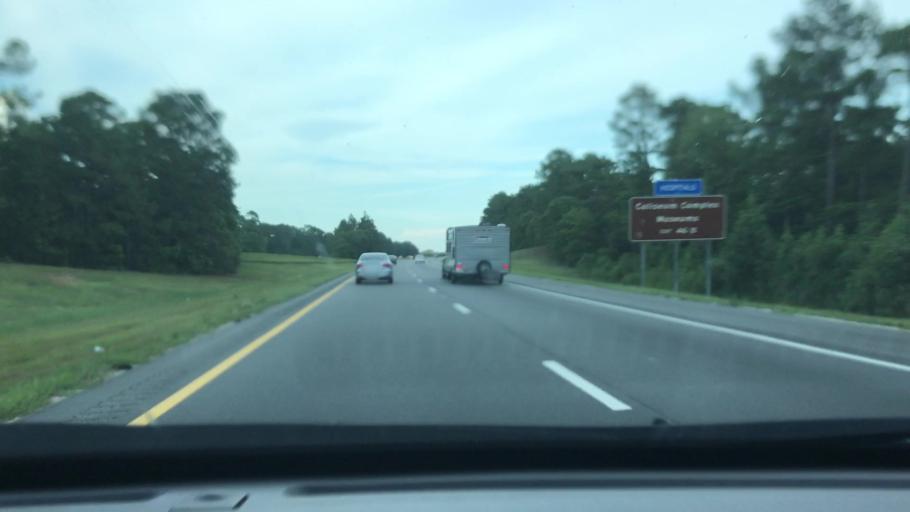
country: US
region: North Carolina
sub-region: Cumberland County
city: Hope Mills
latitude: 34.9688
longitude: -78.8775
